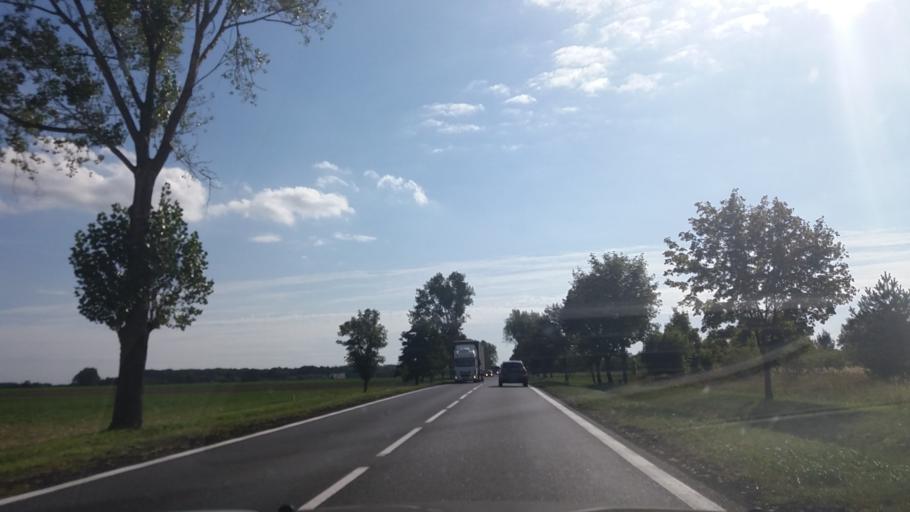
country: PL
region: Lower Silesian Voivodeship
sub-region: Powiat legnicki
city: Prochowice
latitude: 51.3236
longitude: 16.3158
